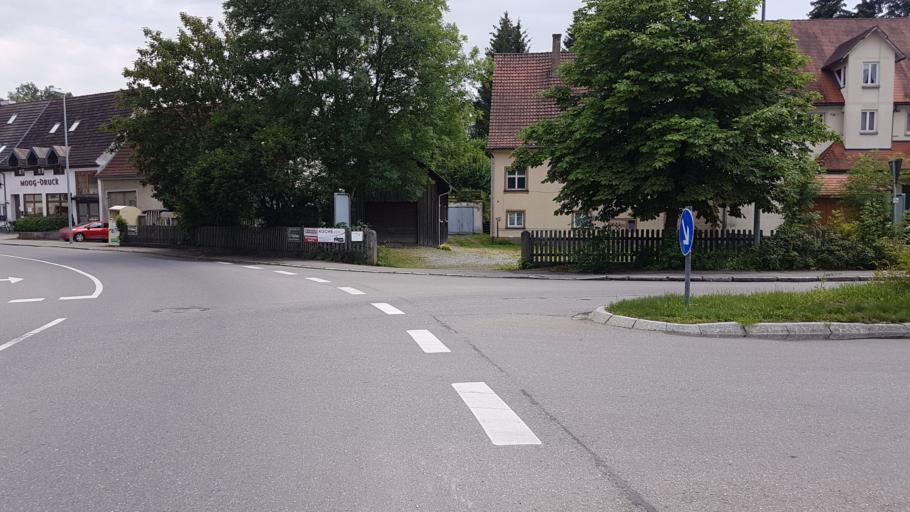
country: DE
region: Baden-Wuerttemberg
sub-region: Freiburg Region
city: Hufingen
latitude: 47.9225
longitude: 8.4887
